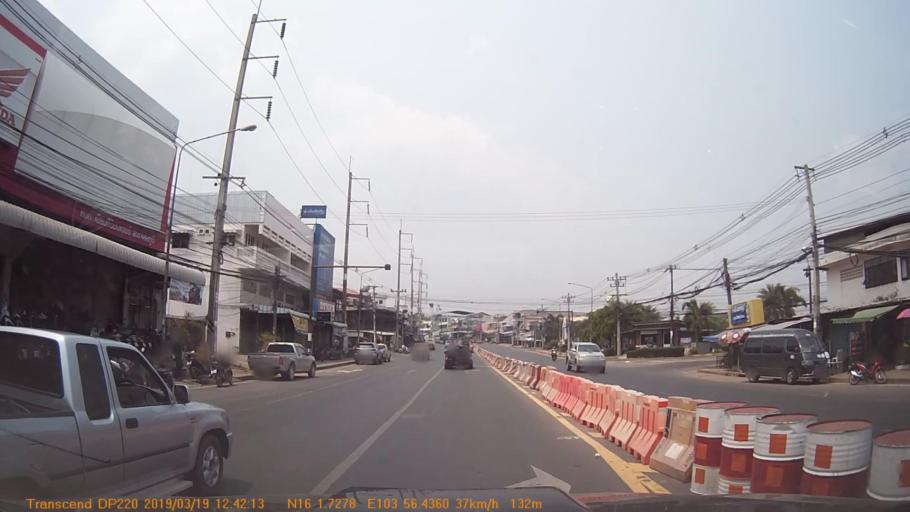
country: TH
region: Roi Et
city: Selaphum
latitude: 16.0290
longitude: 103.9404
